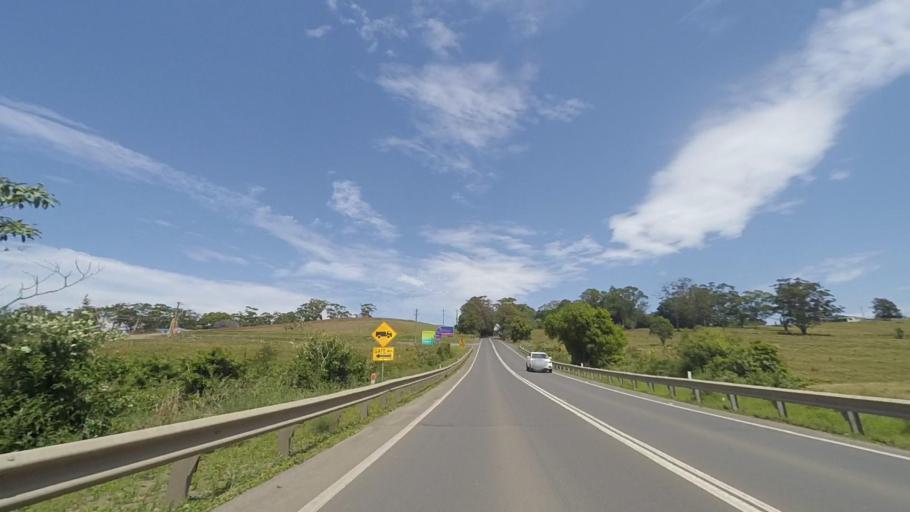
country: AU
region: New South Wales
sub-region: Shoalhaven Shire
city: Berry
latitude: -34.7547
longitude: 150.7492
